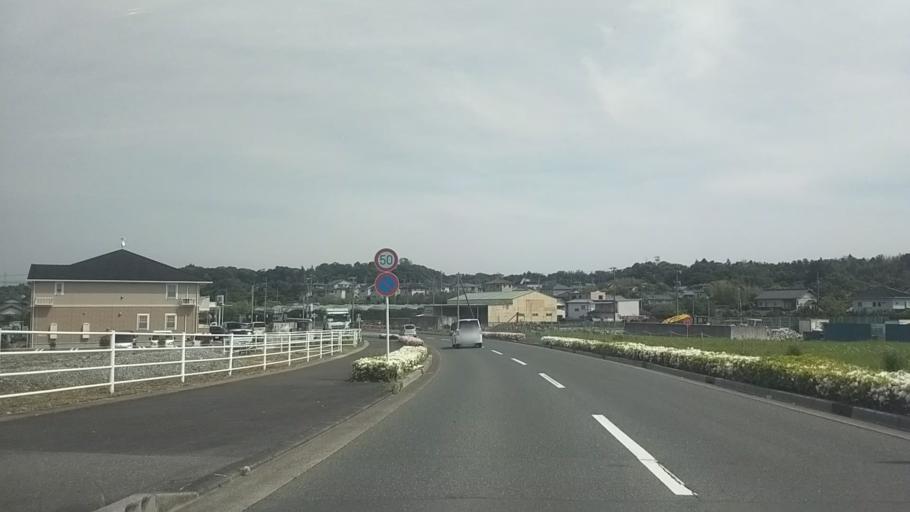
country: JP
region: Shizuoka
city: Hamamatsu
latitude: 34.7940
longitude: 137.6461
